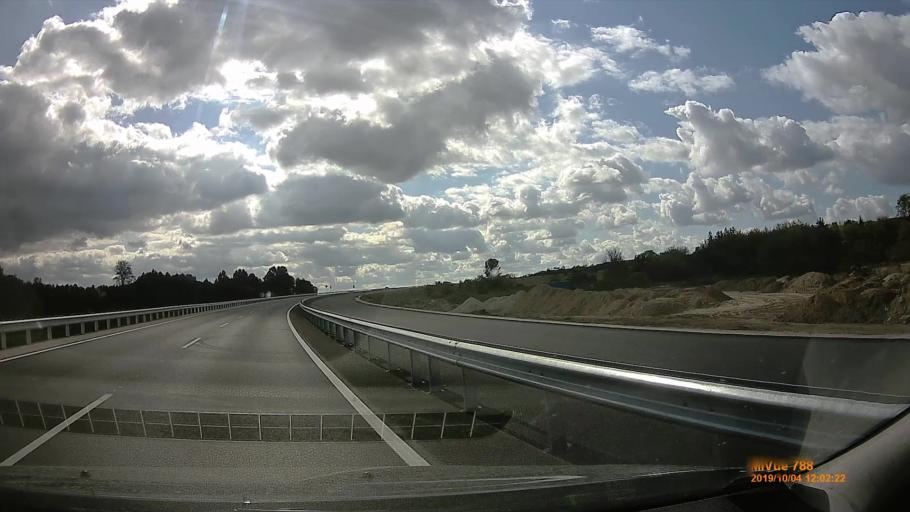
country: HU
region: Somogy
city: Karad
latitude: 46.6014
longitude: 17.8023
